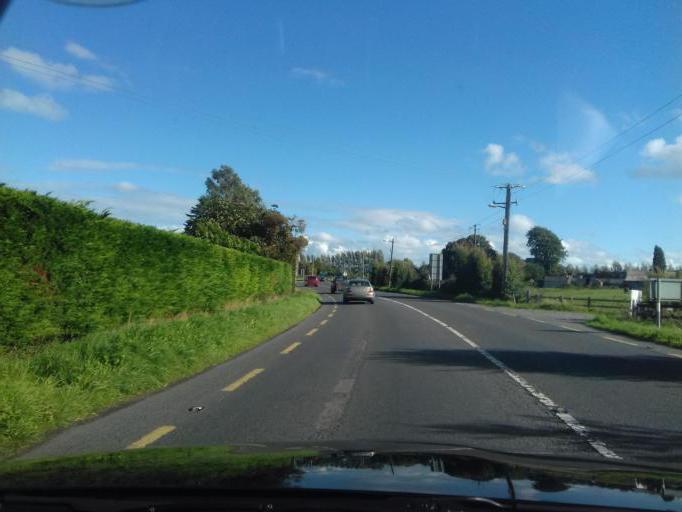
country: IE
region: Leinster
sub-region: Uibh Fhaili
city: Tullamore
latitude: 53.2559
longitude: -7.4816
